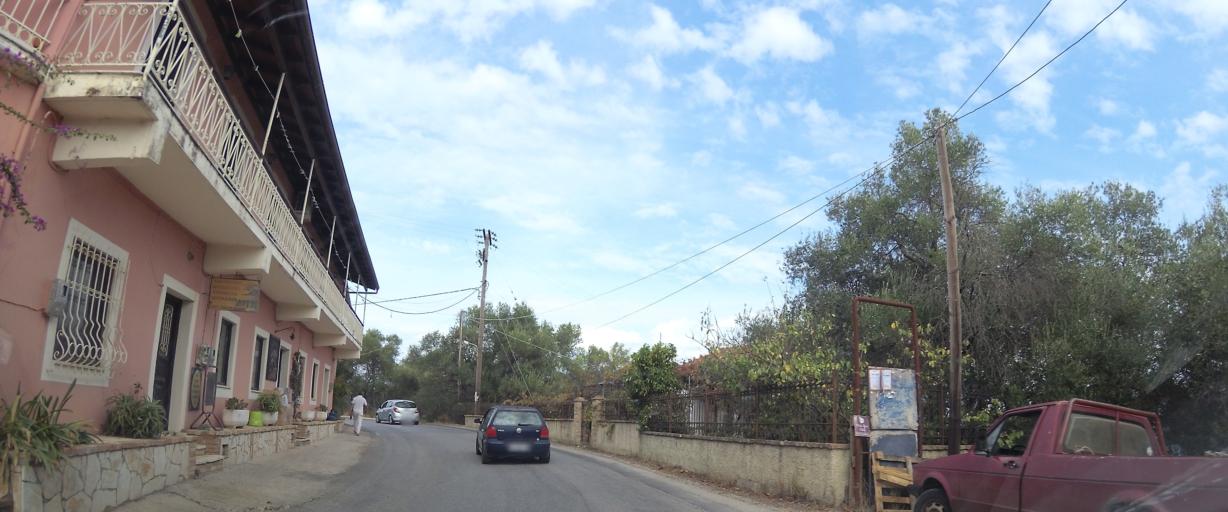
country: GR
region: Ionian Islands
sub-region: Nomos Kerkyras
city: Acharavi
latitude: 39.7584
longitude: 19.9345
